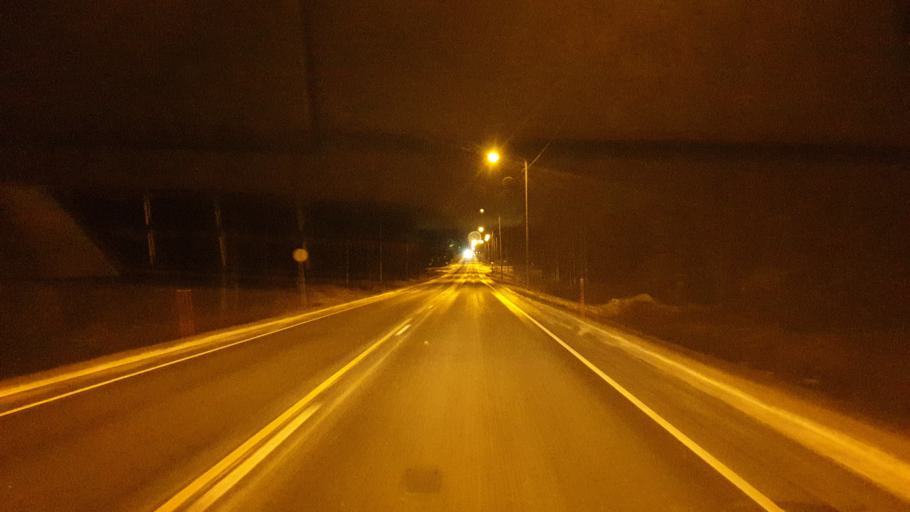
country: FI
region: Central Finland
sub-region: AEaenekoski
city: AEaenekoski
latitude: 62.4887
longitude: 25.6779
